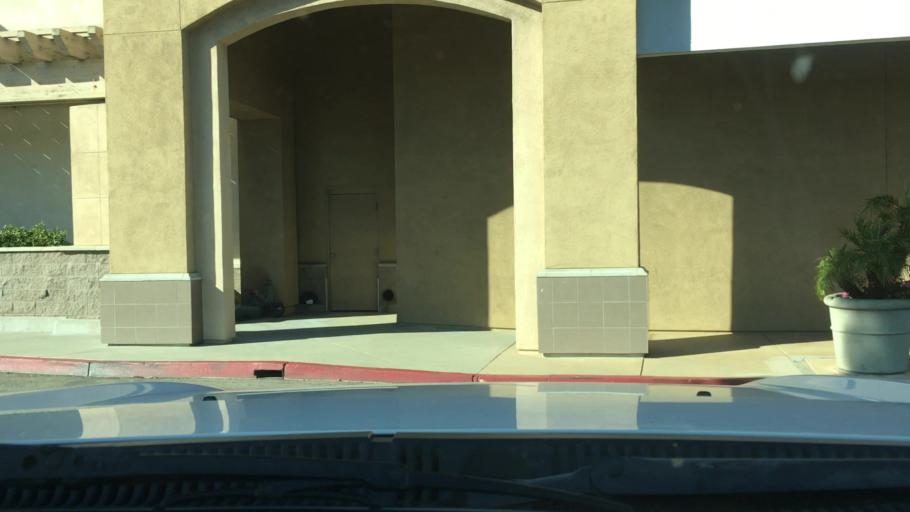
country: US
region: California
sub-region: San Luis Obispo County
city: San Luis Obispo
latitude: 35.2630
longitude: -120.6758
